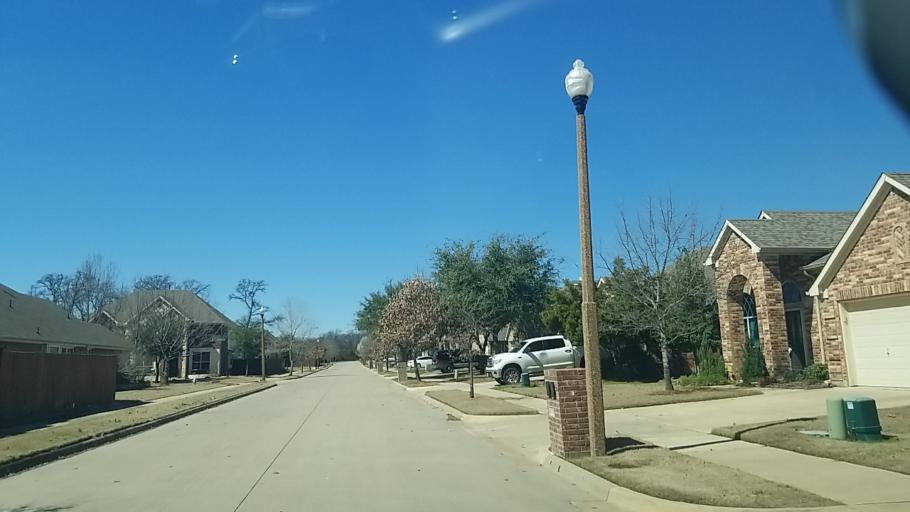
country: US
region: Texas
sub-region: Denton County
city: Corinth
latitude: 33.1574
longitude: -97.1066
